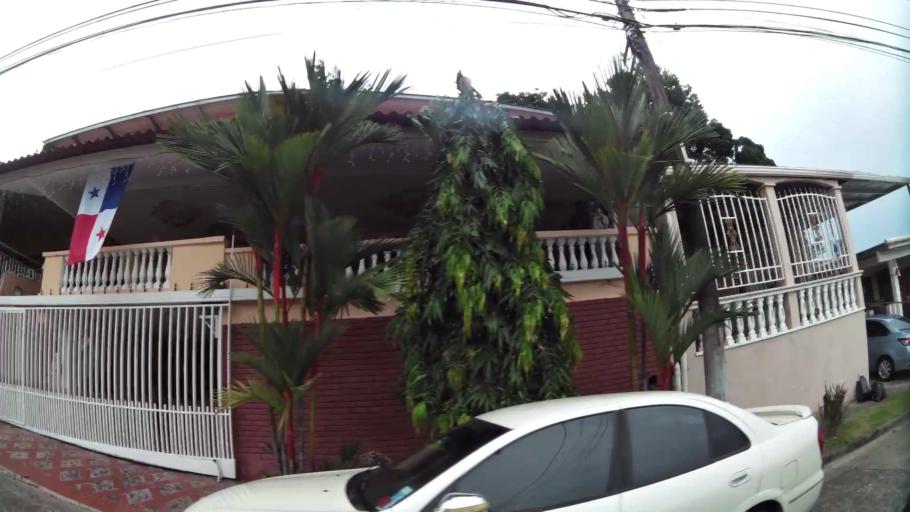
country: PA
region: Panama
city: Panama
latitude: 9.0163
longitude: -79.5292
